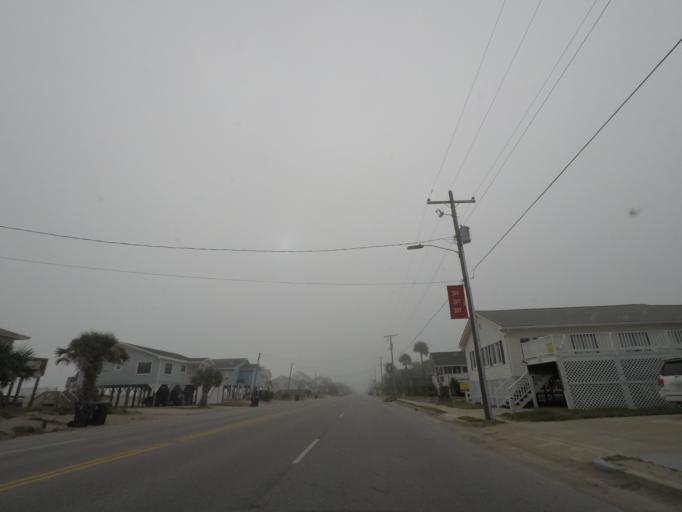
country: US
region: South Carolina
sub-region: Charleston County
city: Seabrook Island
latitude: 32.5015
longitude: -80.2994
